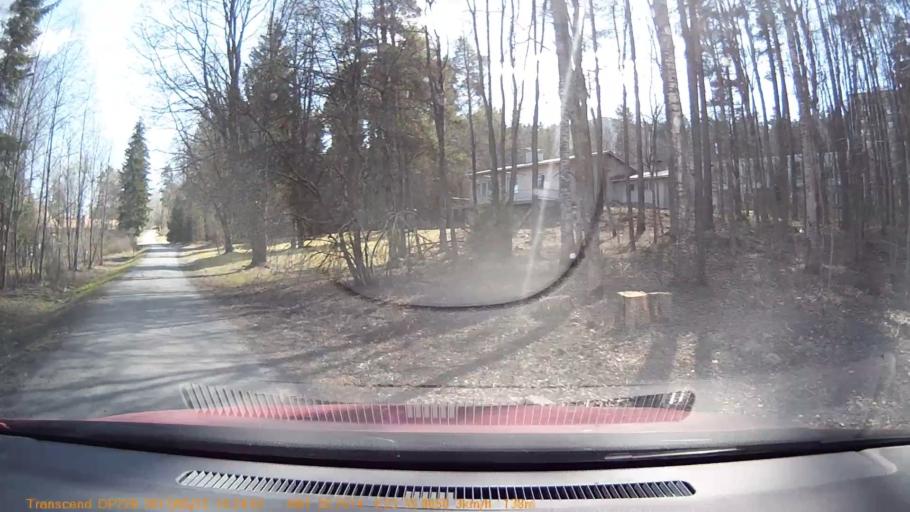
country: FI
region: Pirkanmaa
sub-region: Tampere
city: Yloejaervi
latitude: 61.5459
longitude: 23.5994
